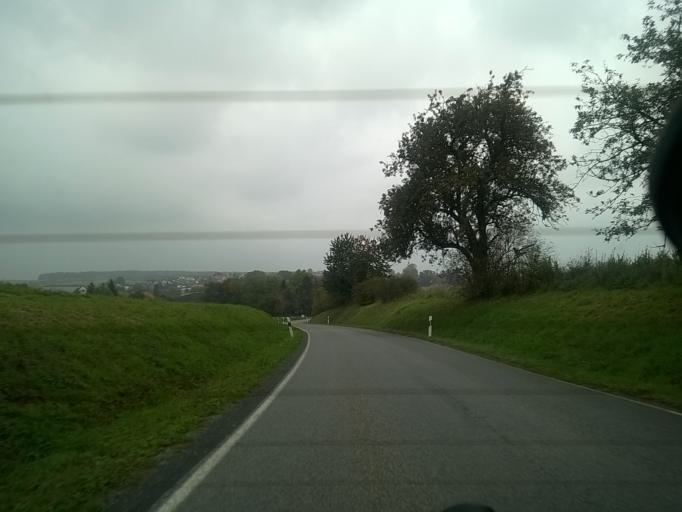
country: DE
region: Baden-Wuerttemberg
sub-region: Regierungsbezirk Stuttgart
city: Bad Rappenau
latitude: 49.2066
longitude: 9.0923
